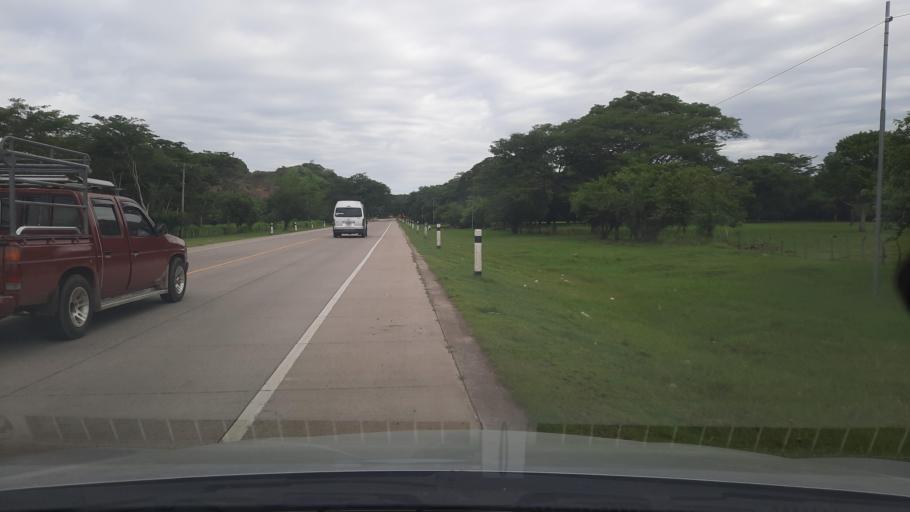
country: NI
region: Chinandega
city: Somotillo
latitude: 12.8713
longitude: -86.8516
